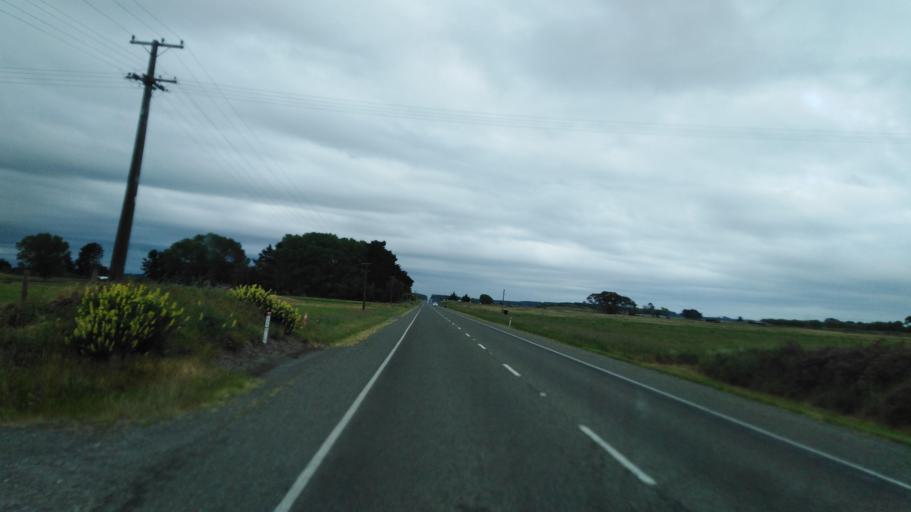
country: NZ
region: Manawatu-Wanganui
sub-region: Horowhenua District
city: Foxton
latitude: -40.3833
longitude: 175.3178
